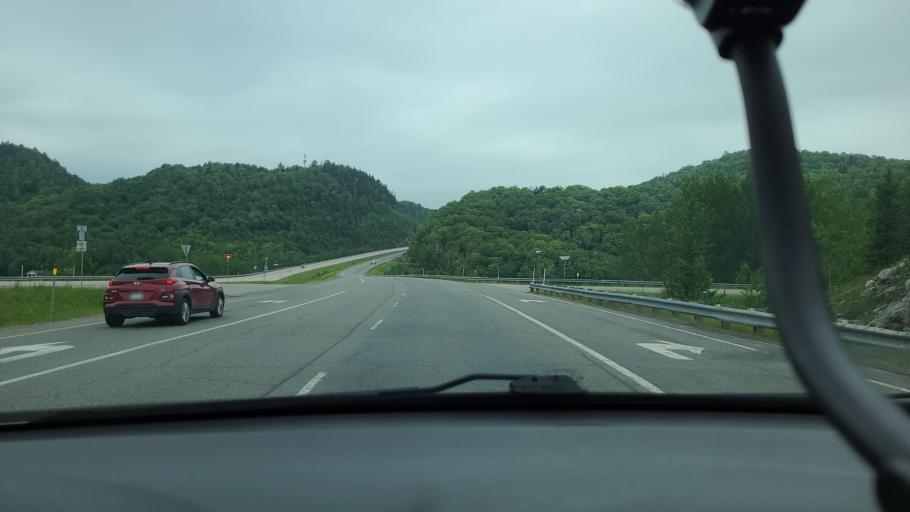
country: CA
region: Quebec
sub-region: Laurentides
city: Mont-Tremblant
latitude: 46.1442
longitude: -74.6527
